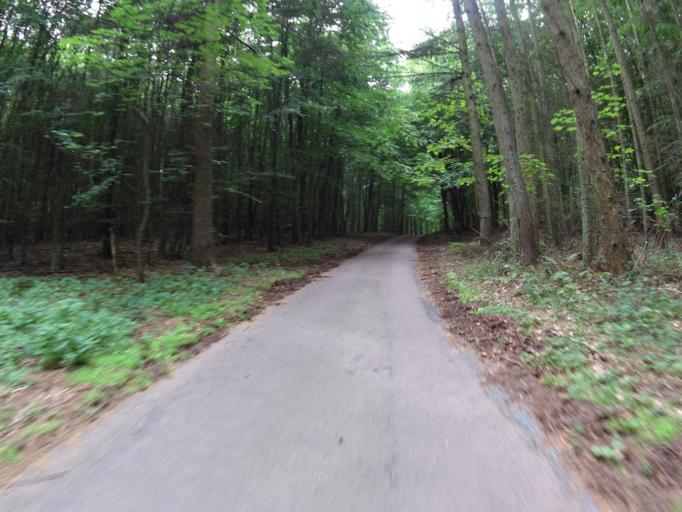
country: DE
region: Mecklenburg-Vorpommern
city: Seebad Heringsdorf
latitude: 53.8998
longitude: 14.1632
